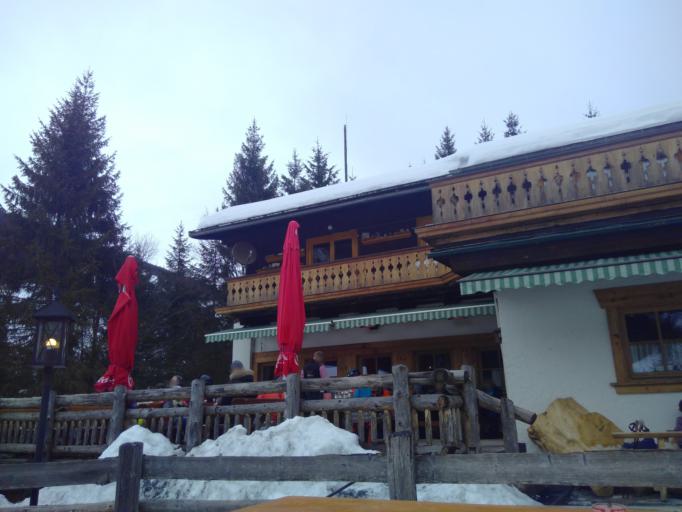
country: AT
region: Salzburg
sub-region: Politischer Bezirk Sankt Johann im Pongau
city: Bad Hofgastein
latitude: 47.1290
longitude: 13.0788
